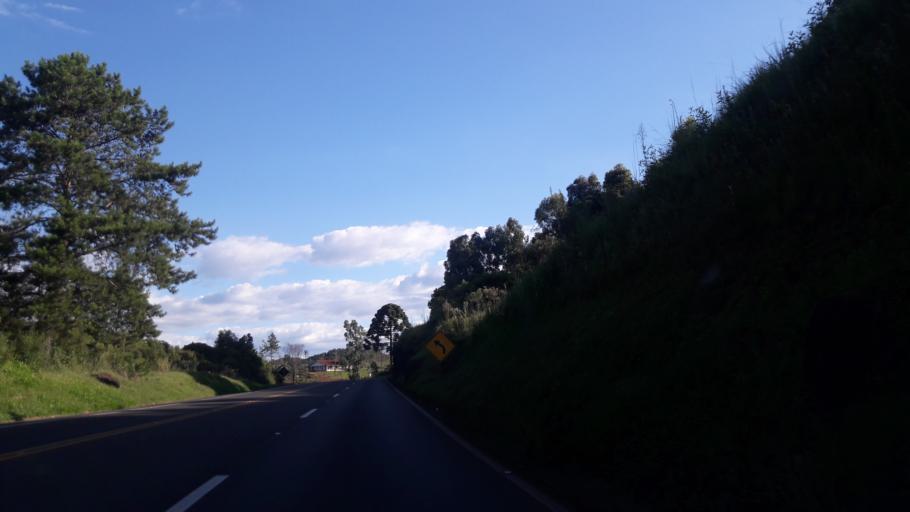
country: BR
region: Parana
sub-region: Guarapuava
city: Guarapuava
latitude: -25.3634
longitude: -51.3497
